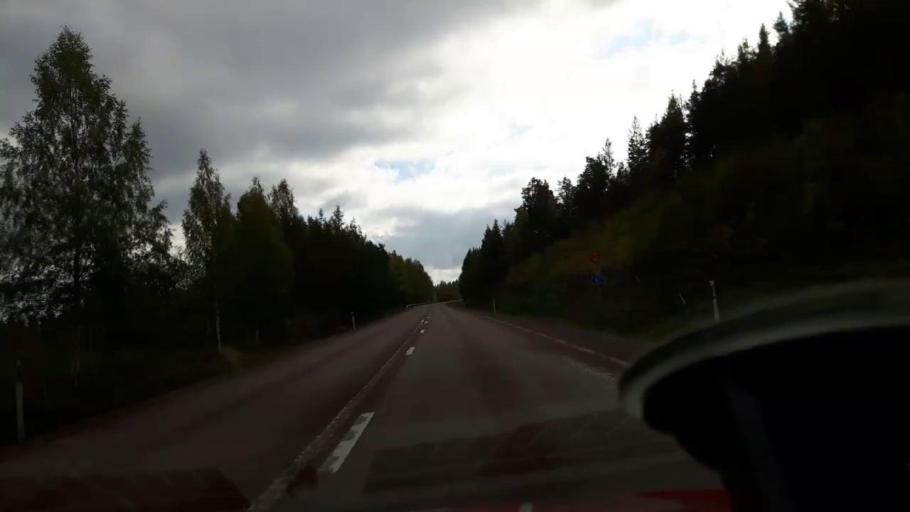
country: SE
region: Gaevleborg
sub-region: Bollnas Kommun
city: Arbra
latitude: 61.5933
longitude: 16.3009
